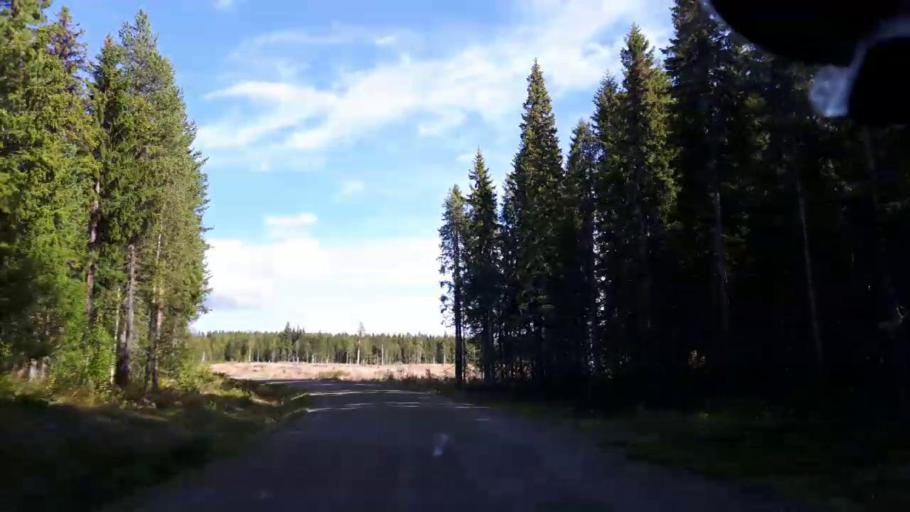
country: SE
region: Jaemtland
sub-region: Ragunda Kommun
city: Hammarstrand
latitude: 63.4419
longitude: 15.9576
